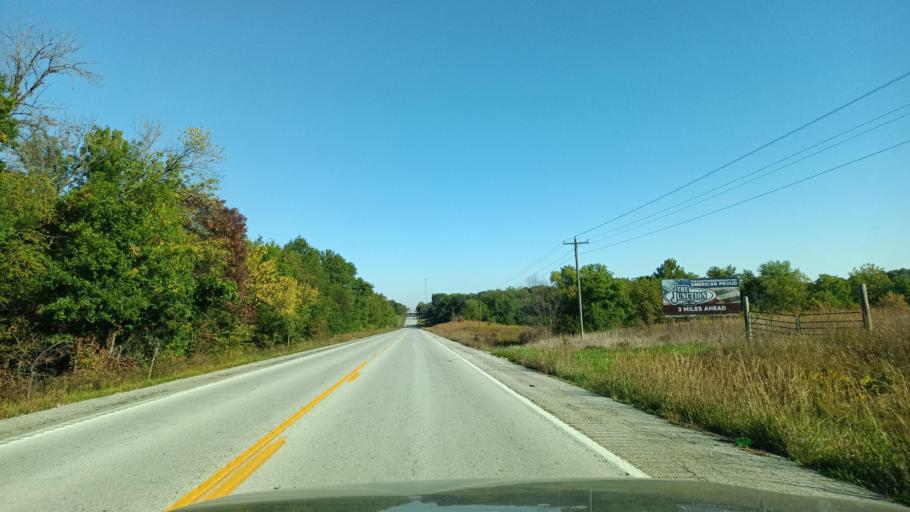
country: US
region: Missouri
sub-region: Audrain County
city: Vandalia
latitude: 39.3861
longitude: -91.6419
